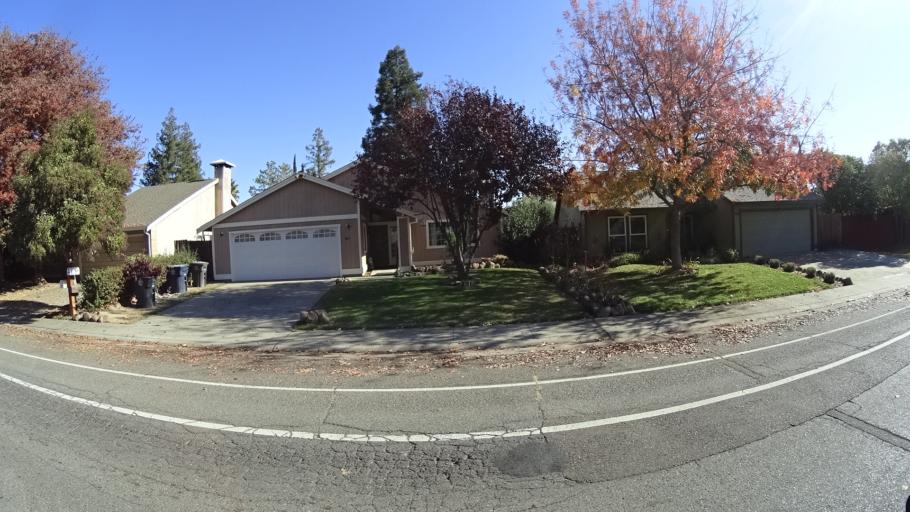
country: US
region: California
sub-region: Sacramento County
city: Antelope
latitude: 38.7111
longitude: -121.3113
